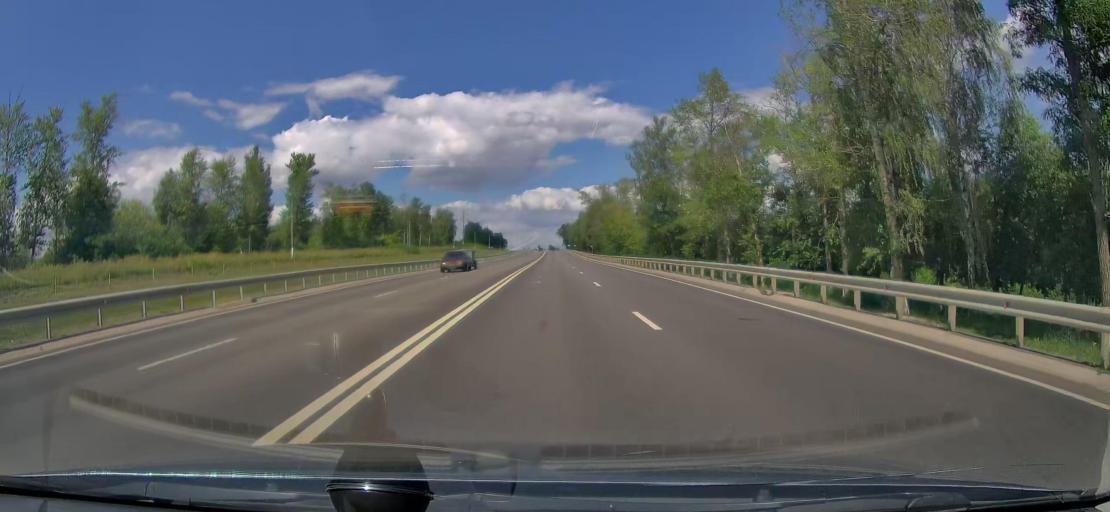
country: RU
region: Kursk
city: Zolotukhino
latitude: 51.9557
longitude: 36.3051
